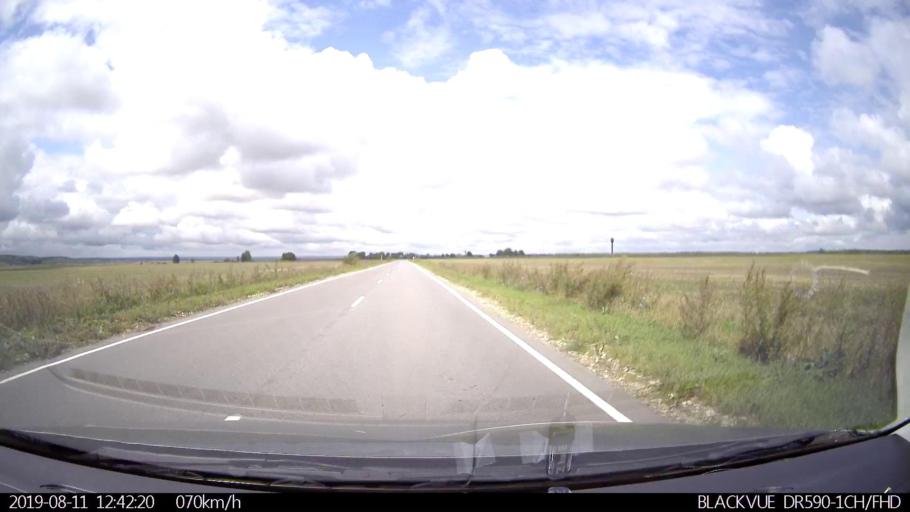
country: RU
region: Ulyanovsk
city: Ignatovka
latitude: 53.8451
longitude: 47.7527
